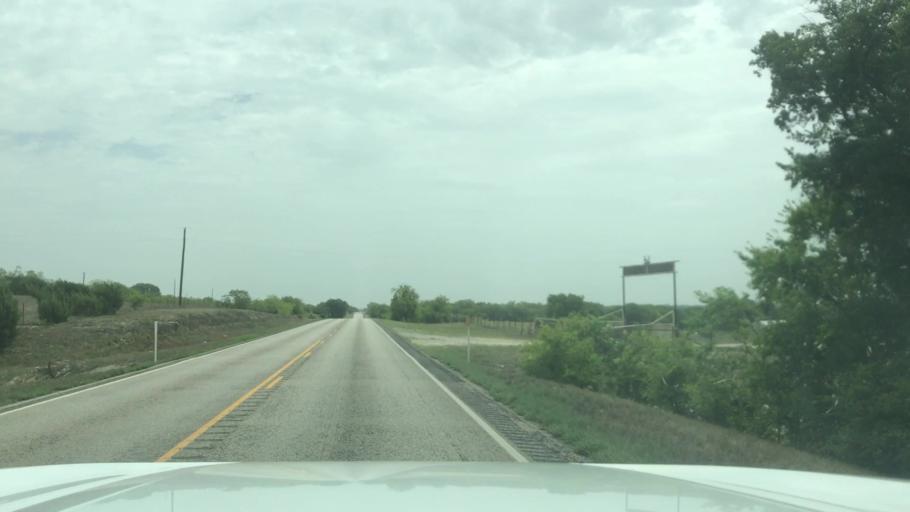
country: US
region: Texas
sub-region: Hamilton County
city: Hico
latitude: 32.0503
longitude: -98.1612
